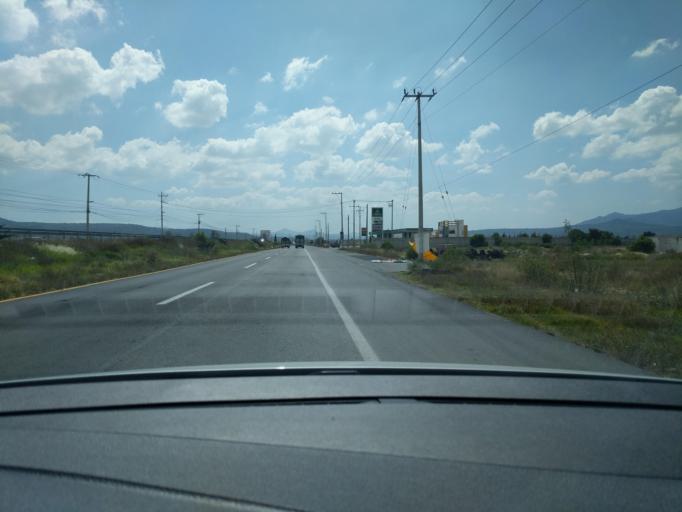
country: MX
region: Hidalgo
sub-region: Mineral de la Reforma
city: Rinconada de los Angeles
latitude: 20.0265
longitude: -98.7255
